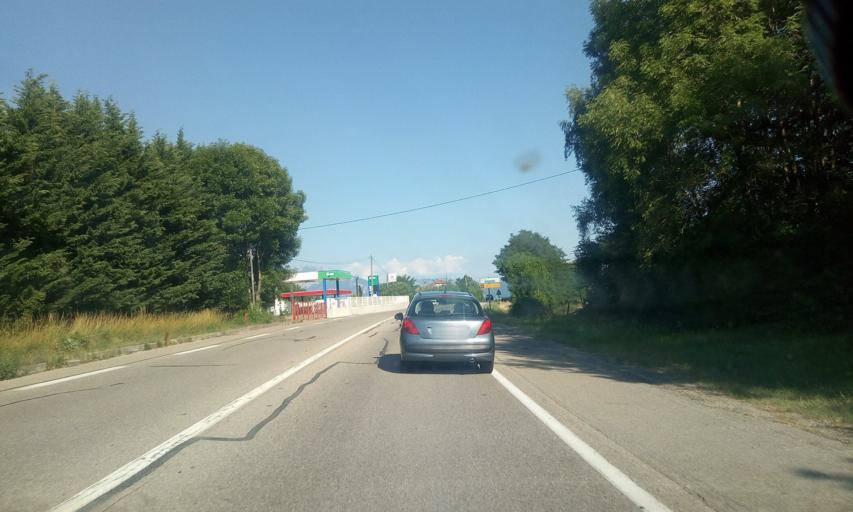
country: FR
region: Rhone-Alpes
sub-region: Departement de l'Isere
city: Beaucroissant
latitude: 45.3460
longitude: 5.4780
